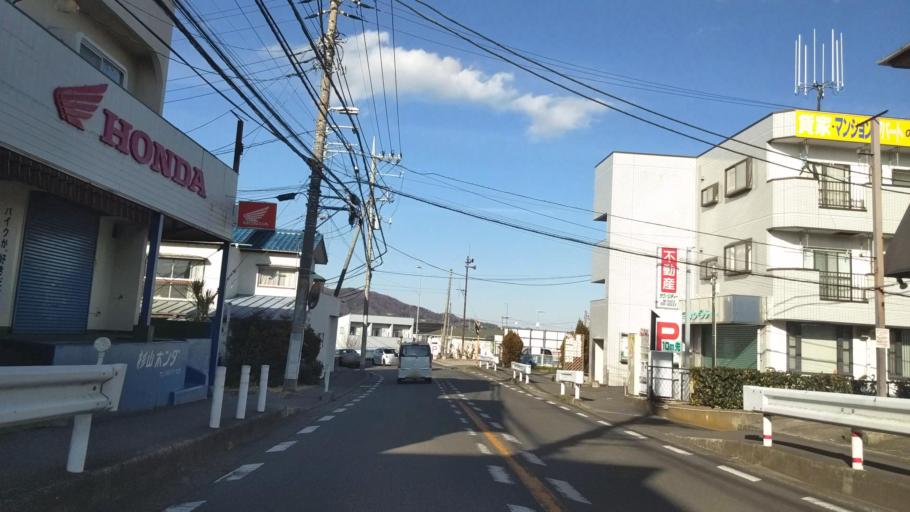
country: JP
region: Kanagawa
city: Isehara
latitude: 35.3685
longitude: 139.2739
